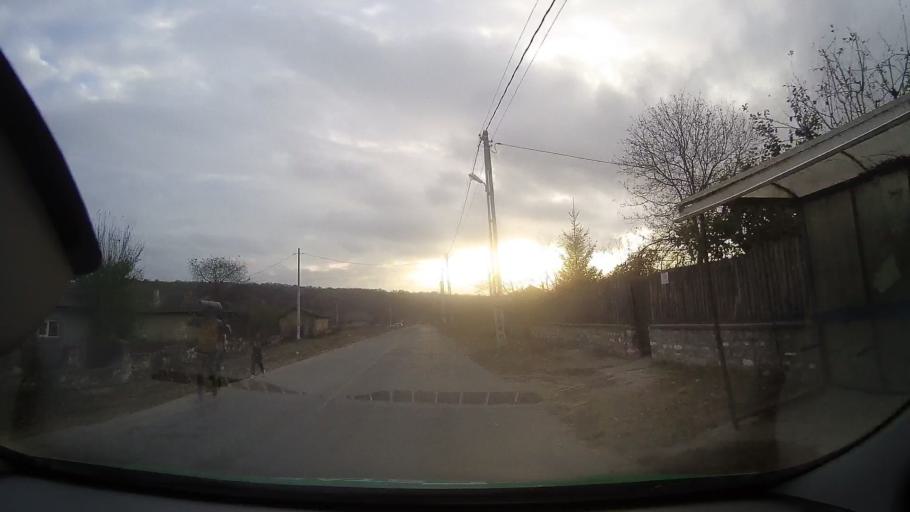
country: RO
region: Constanta
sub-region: Comuna Adamclisi
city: Adamclisi
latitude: 44.0421
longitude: 27.9548
